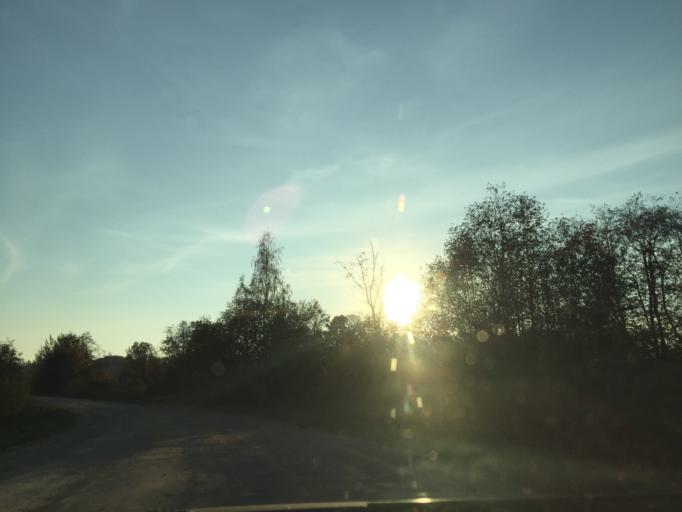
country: LV
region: Vainode
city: Vainode
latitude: 56.5096
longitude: 21.8258
